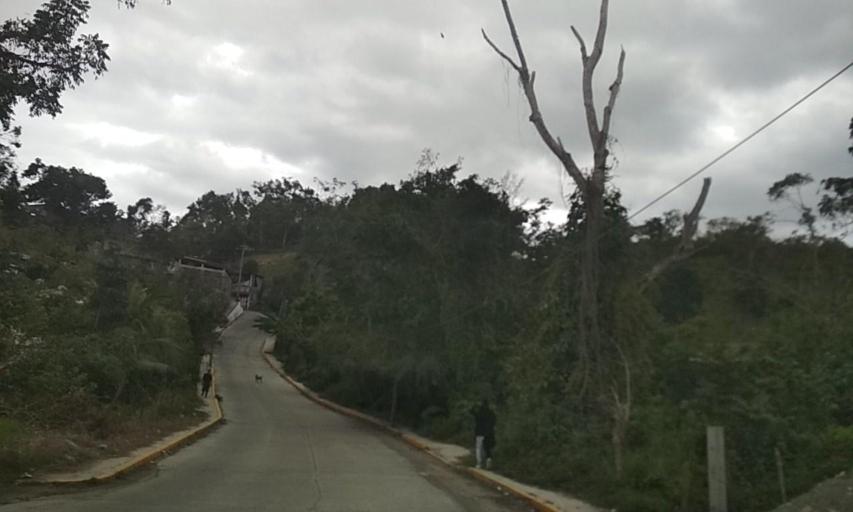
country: MX
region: Veracruz
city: Papantla de Olarte
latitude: 20.4598
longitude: -97.3188
